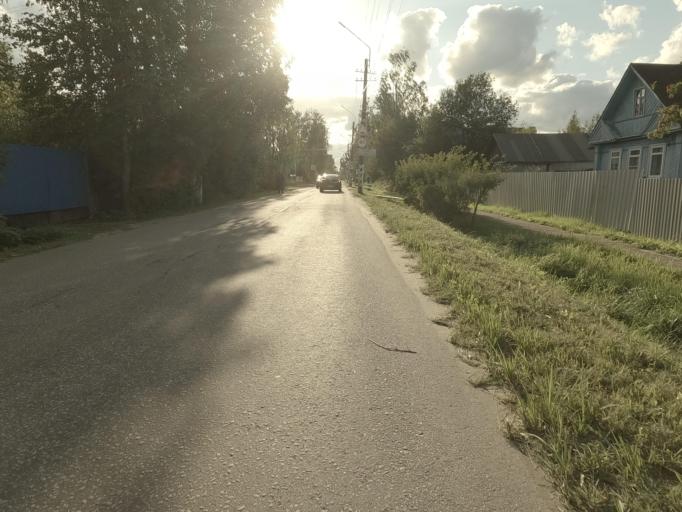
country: RU
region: Leningrad
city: Mga
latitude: 59.7574
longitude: 31.0708
